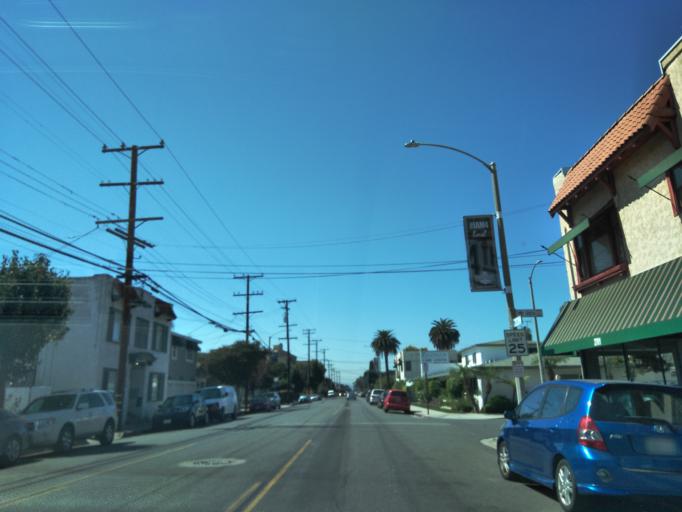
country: US
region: California
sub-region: Los Angeles County
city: Long Beach
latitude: 33.7718
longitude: -118.1599
